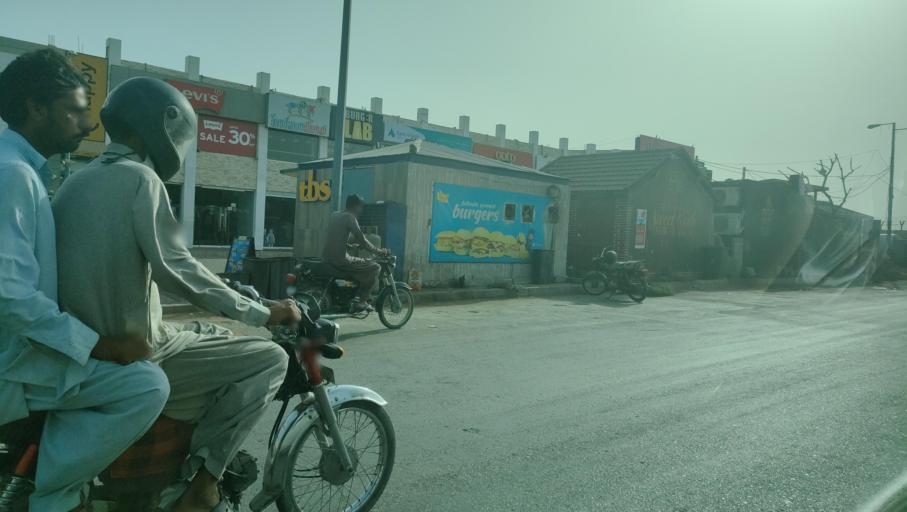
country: PK
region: Sindh
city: Malir Cantonment
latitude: 24.9224
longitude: 67.1842
